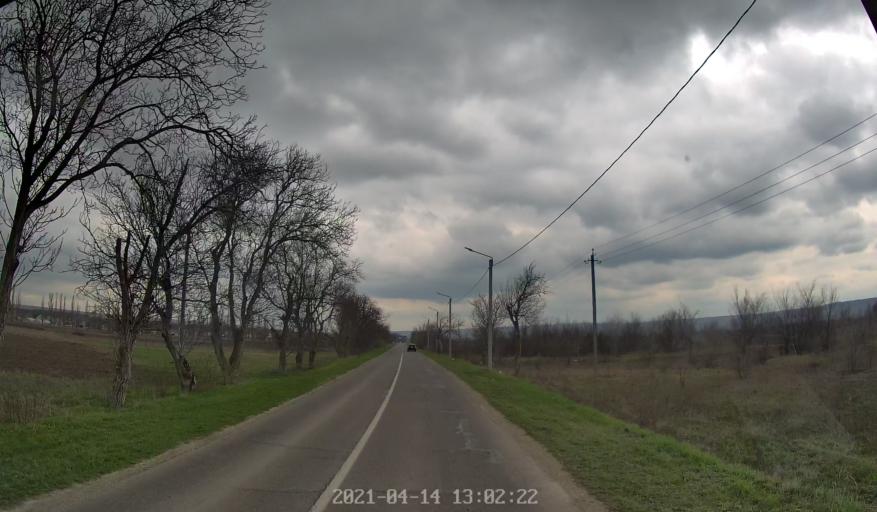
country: MD
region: Chisinau
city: Vadul lui Voda
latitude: 47.1240
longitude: 29.1110
